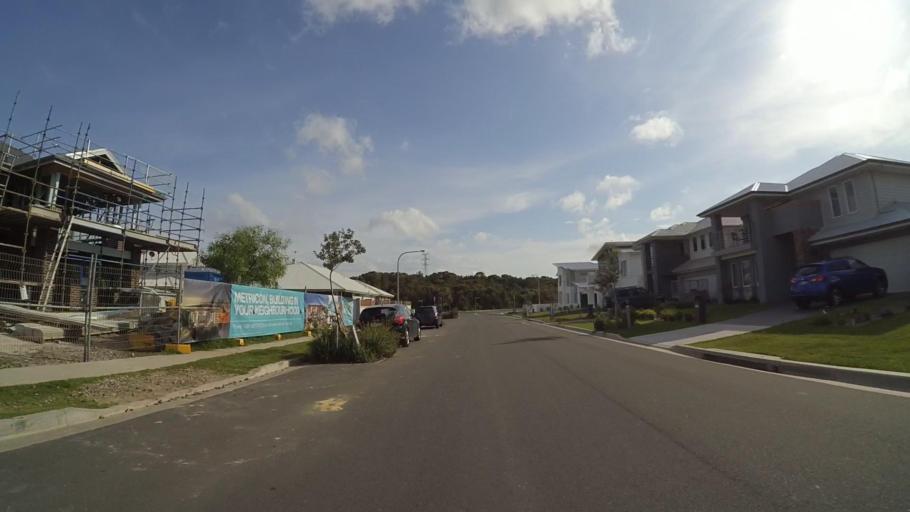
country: AU
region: New South Wales
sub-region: Sutherland Shire
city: Cronulla
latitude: -34.0348
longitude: 151.1625
